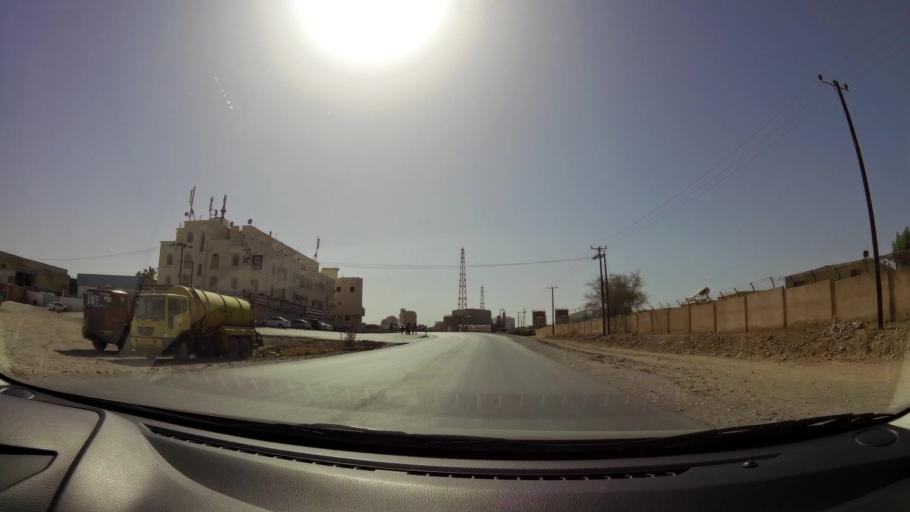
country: OM
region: Muhafazat Masqat
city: Bawshar
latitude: 23.5772
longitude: 58.3505
